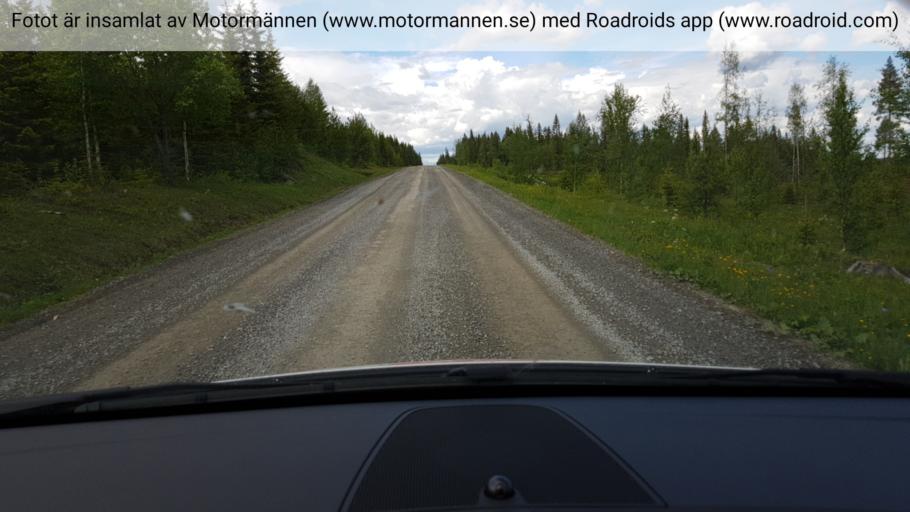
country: SE
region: Jaemtland
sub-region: Bergs Kommun
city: Hoverberg
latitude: 63.0057
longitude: 14.1283
